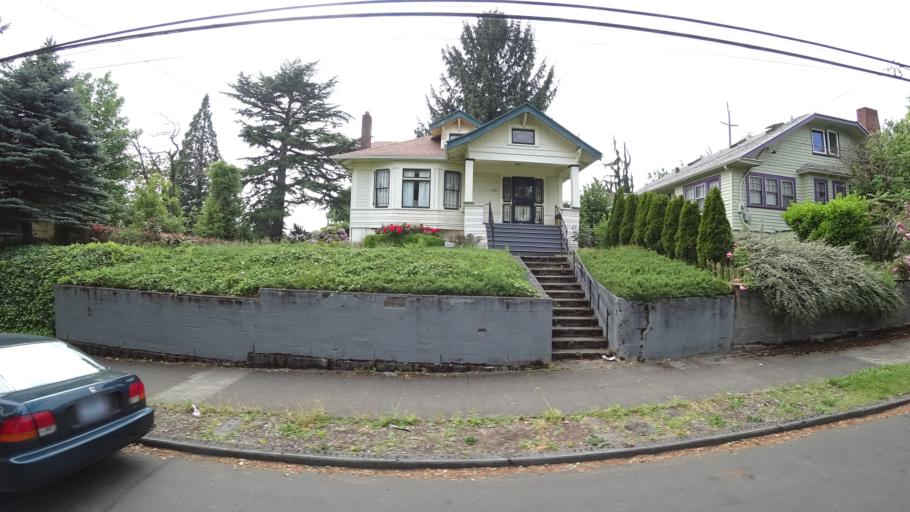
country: US
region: Oregon
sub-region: Multnomah County
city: Portland
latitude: 45.5561
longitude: -122.6537
